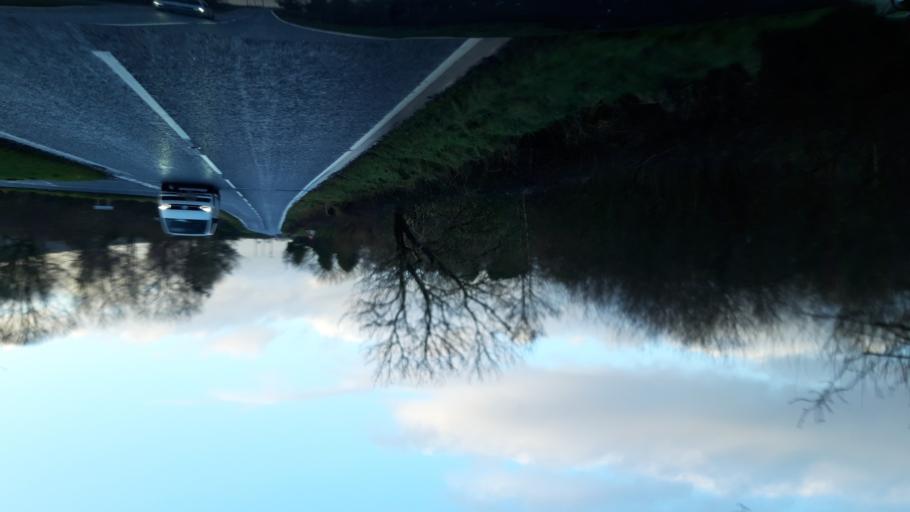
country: GB
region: Northern Ireland
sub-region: Moyle District
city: Ballycastle
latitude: 55.1168
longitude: -6.3347
